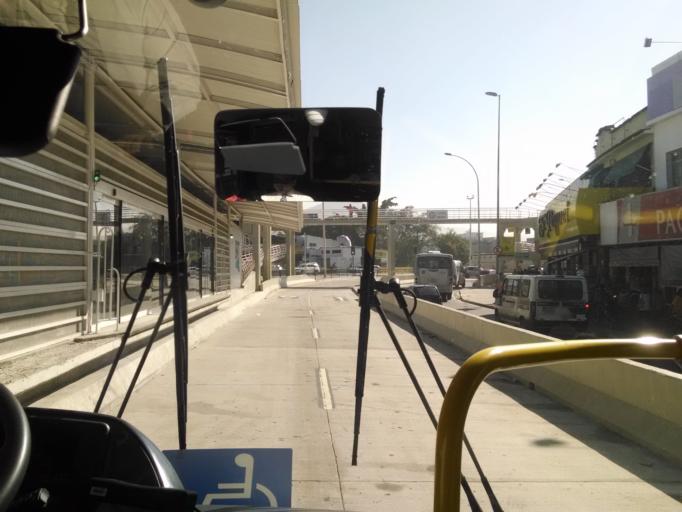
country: BR
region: Rio de Janeiro
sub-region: Sao Joao De Meriti
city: Sao Joao de Meriti
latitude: -22.9238
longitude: -43.3738
